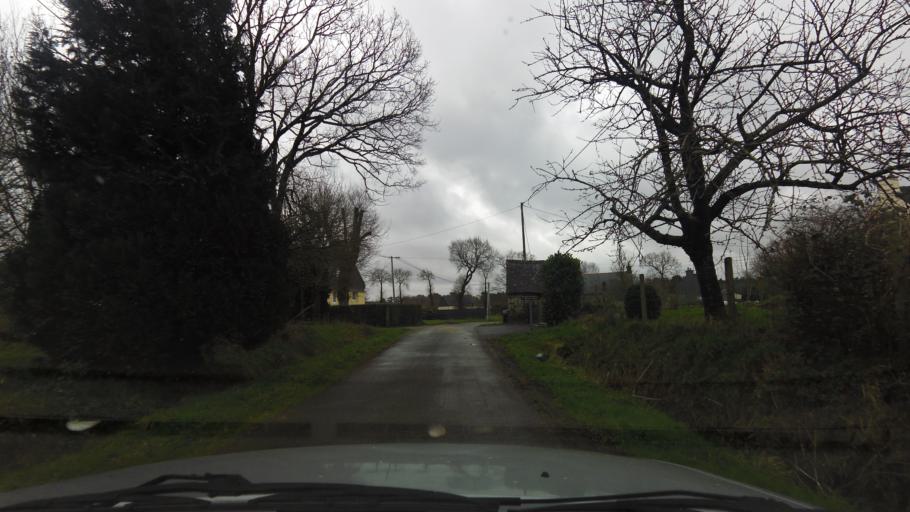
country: FR
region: Brittany
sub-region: Departement du Morbihan
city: Molac
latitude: 47.7729
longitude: -2.4713
